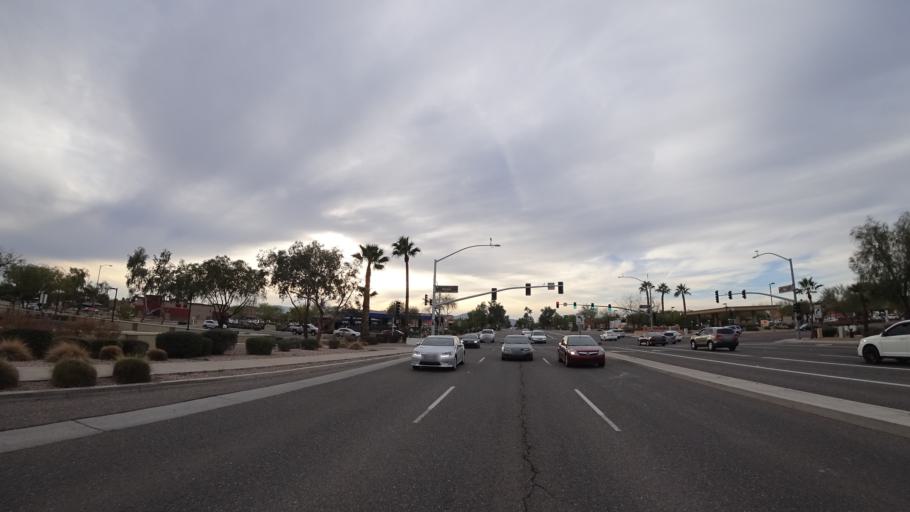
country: US
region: Arizona
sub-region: Maricopa County
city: Sun City West
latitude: 33.6386
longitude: -112.3937
